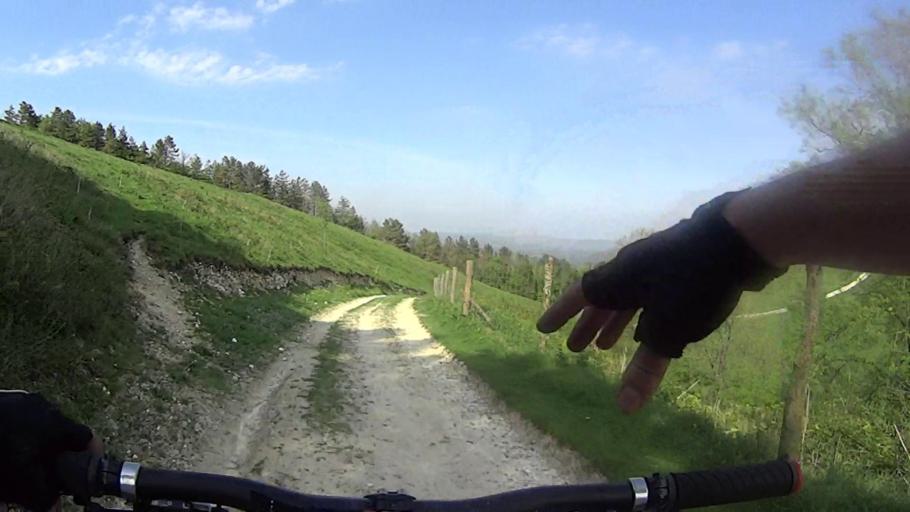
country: GB
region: England
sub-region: West Sussex
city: Milland
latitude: 50.9580
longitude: -0.8498
